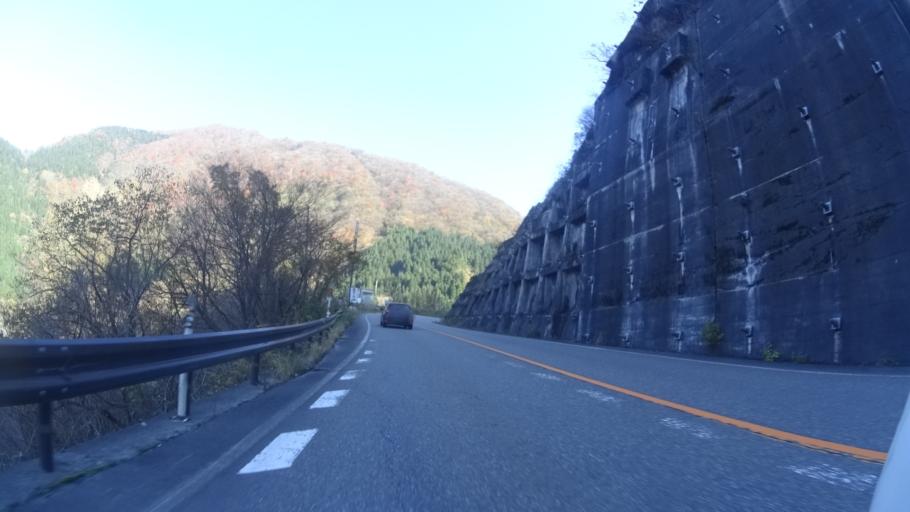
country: JP
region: Fukui
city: Ono
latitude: 35.9551
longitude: 136.6199
